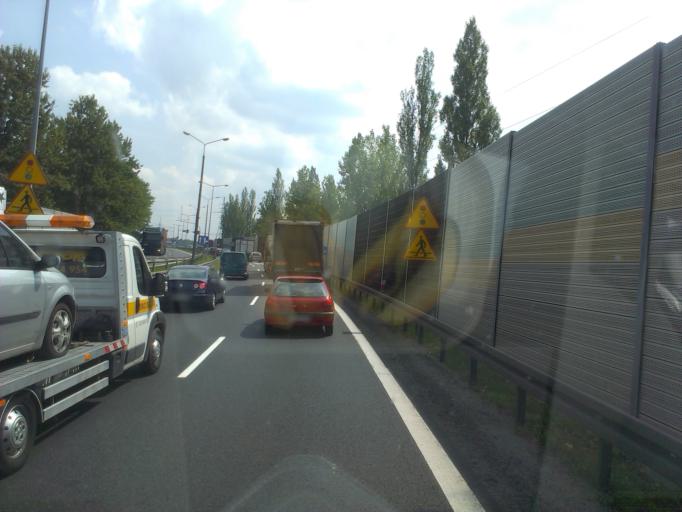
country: PL
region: Lower Silesian Voivodeship
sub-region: Powiat polkowicki
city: Polkowice
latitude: 51.4979
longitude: 16.0643
